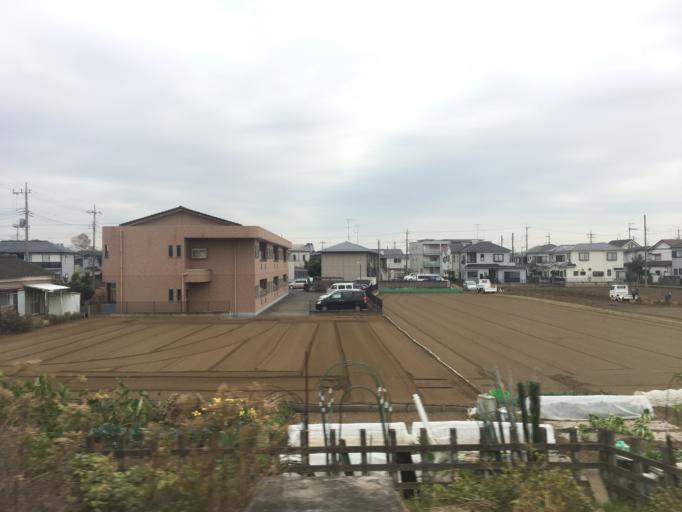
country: JP
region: Saitama
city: Kawagoe
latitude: 35.8929
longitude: 139.4956
